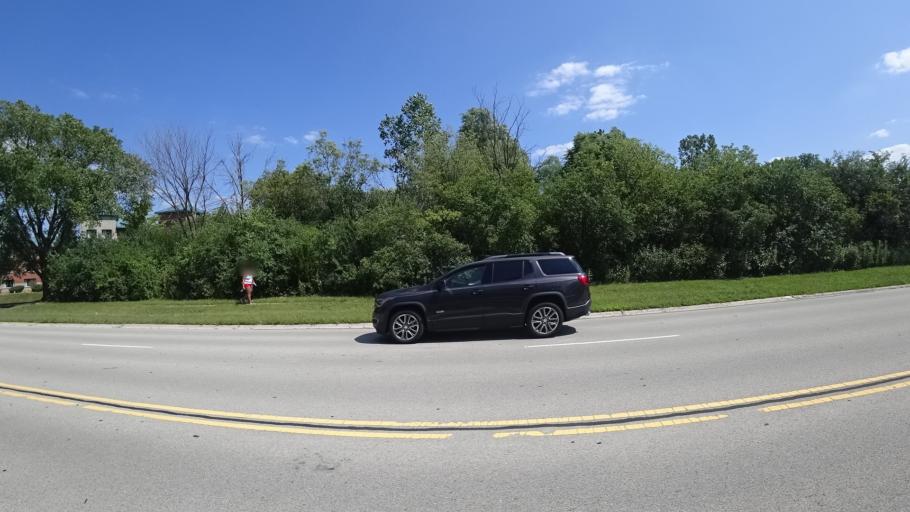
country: US
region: Illinois
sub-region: Cook County
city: Orland Park
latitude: 41.6241
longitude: -87.8514
